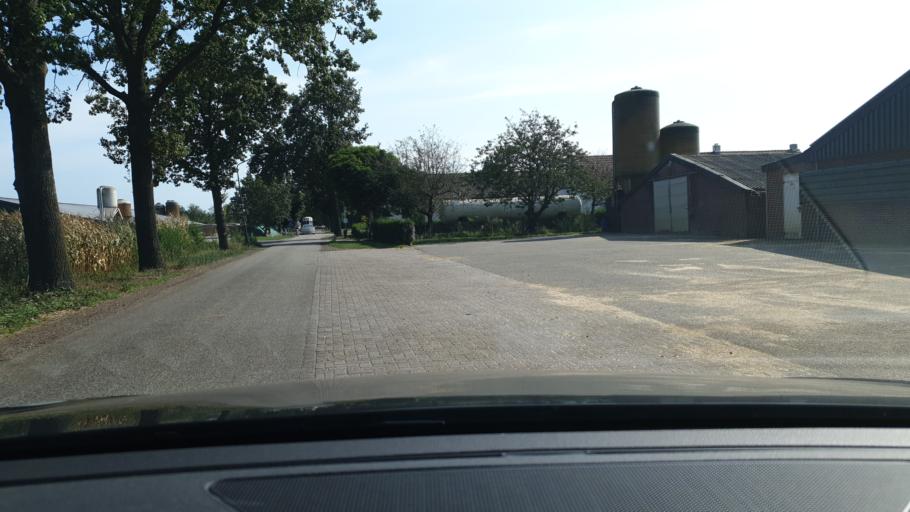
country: NL
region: North Brabant
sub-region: Gemeente Boekel
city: Boekel
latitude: 51.5580
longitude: 5.7404
